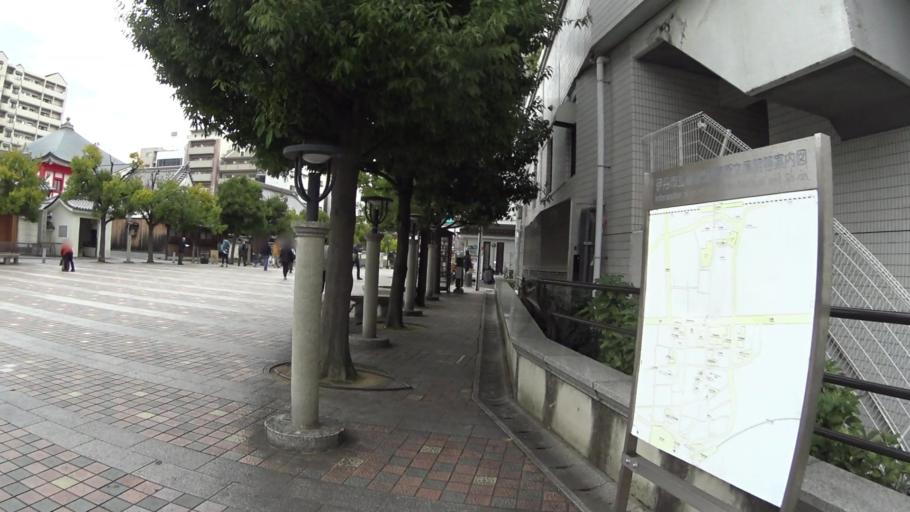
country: JP
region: Hyogo
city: Itami
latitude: 34.7810
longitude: 135.4156
